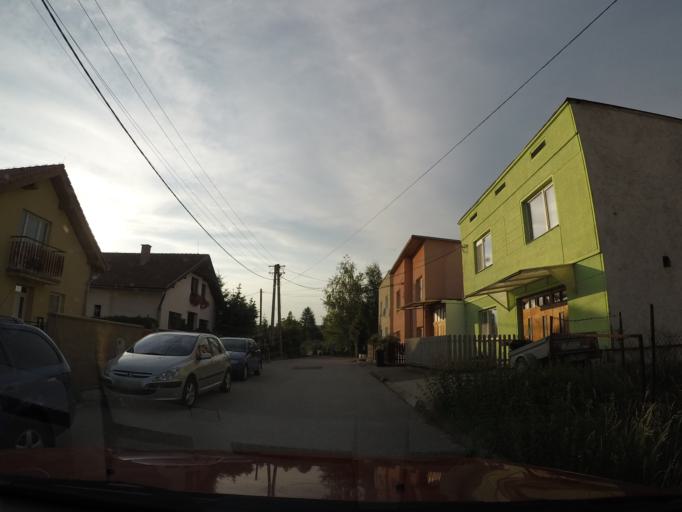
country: SK
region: Kosicky
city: Kosice
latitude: 48.7055
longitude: 21.2152
